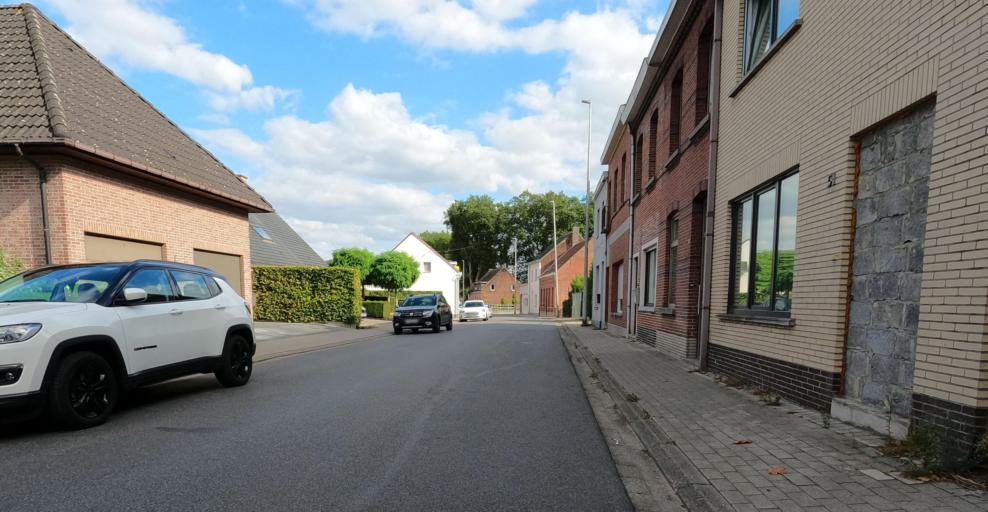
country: BE
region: Flanders
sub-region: Provincie Oost-Vlaanderen
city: Dendermonde
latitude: 51.0186
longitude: 4.0877
